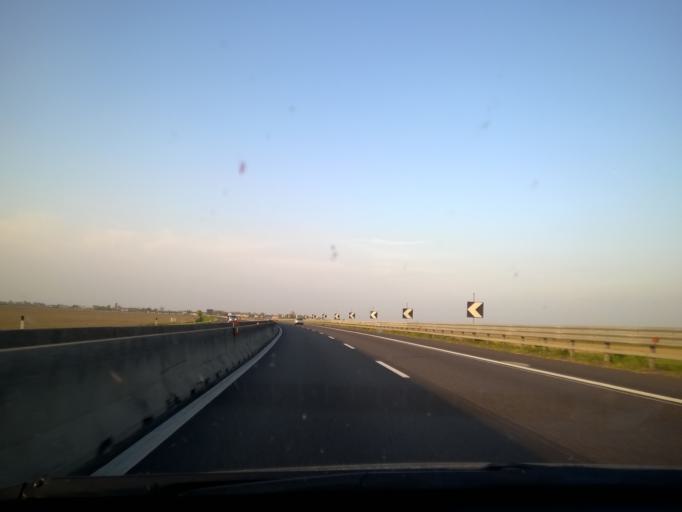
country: IT
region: Veneto
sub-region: Provincia di Rovigo
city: Fiesso Umbertiano
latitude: 44.9487
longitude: 11.6358
